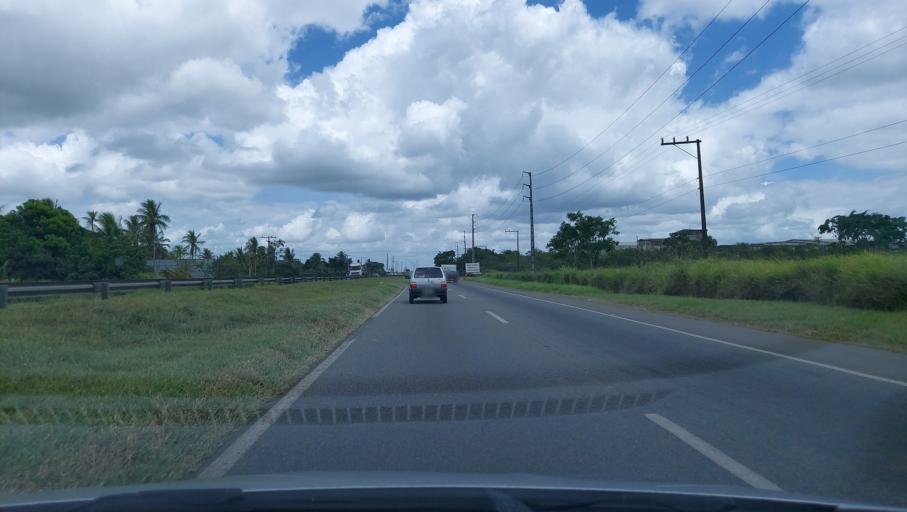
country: BR
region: Bahia
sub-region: Conceicao Do Jacuipe
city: Conceicao do Jacuipe
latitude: -12.3732
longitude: -38.8085
